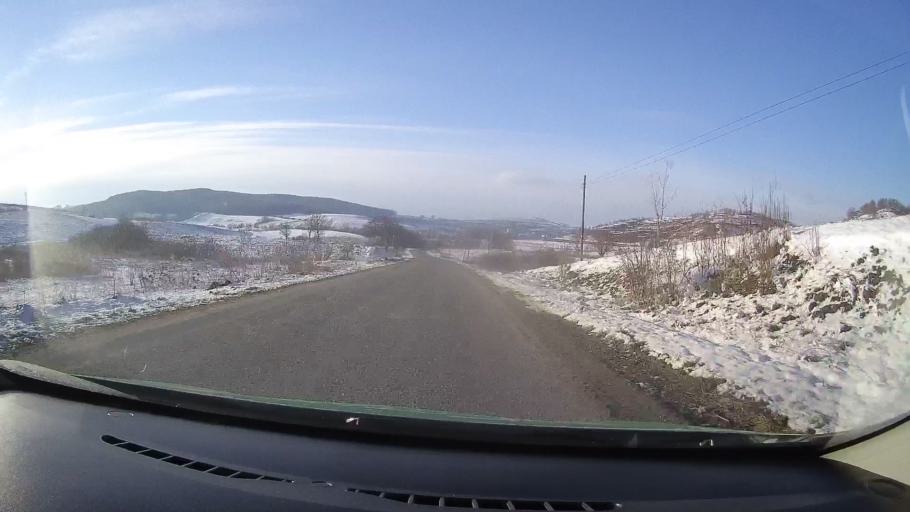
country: RO
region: Sibiu
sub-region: Comuna Merghindeal
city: Merghindeal
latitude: 45.9699
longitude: 24.7100
